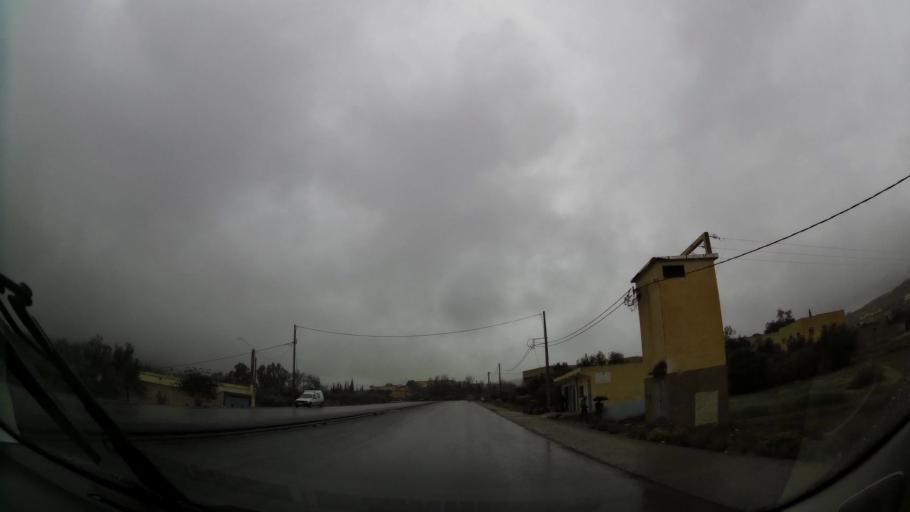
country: MA
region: Taza-Al Hoceima-Taounate
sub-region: Taza
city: Aknoul
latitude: 34.8112
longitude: -3.7340
